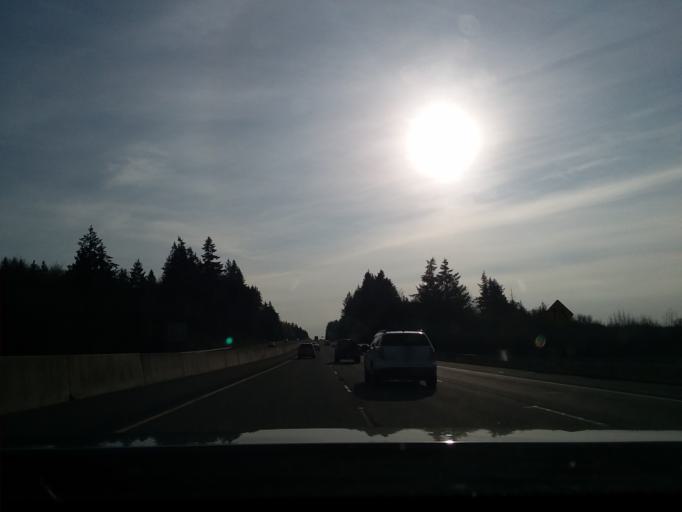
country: US
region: Washington
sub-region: Thurston County
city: Tenino
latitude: 46.8942
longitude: -122.9617
